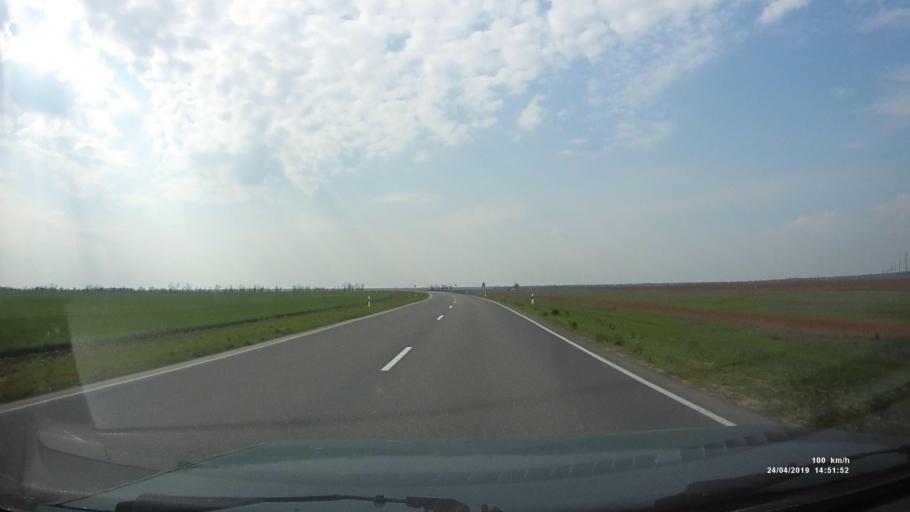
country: RU
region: Rostov
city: Remontnoye
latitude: 46.5281
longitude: 43.6926
